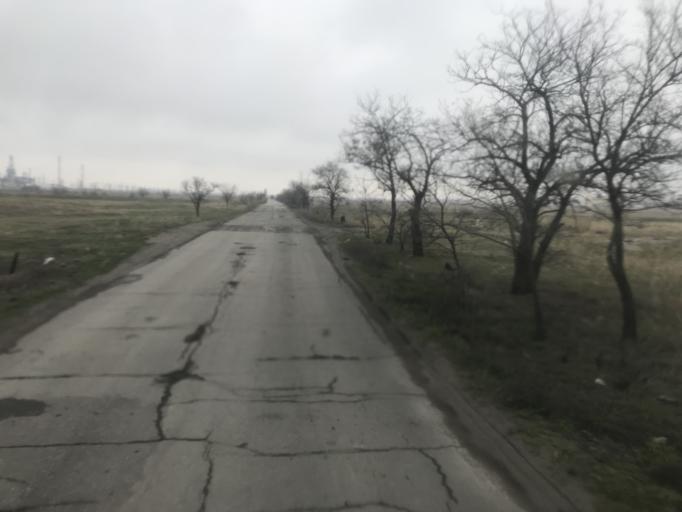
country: RU
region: Volgograd
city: Svetlyy Yar
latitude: 48.4978
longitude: 44.6494
